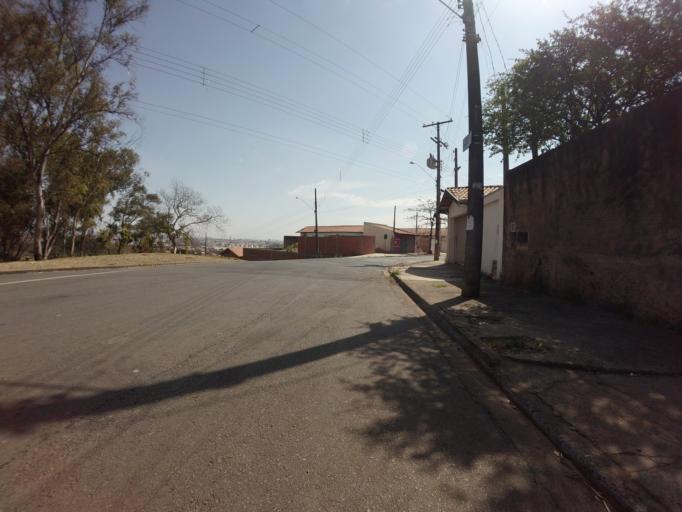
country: BR
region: Sao Paulo
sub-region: Piracicaba
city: Piracicaba
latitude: -22.7598
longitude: -47.5994
